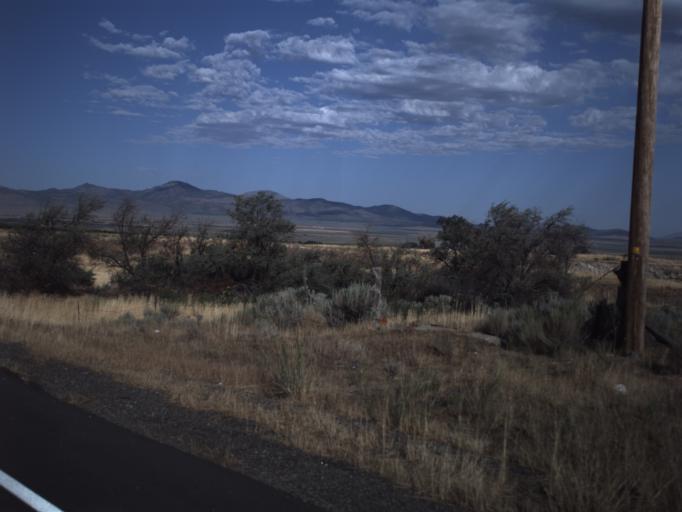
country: US
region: Utah
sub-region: Utah County
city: Genola
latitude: 39.9851
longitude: -111.8207
